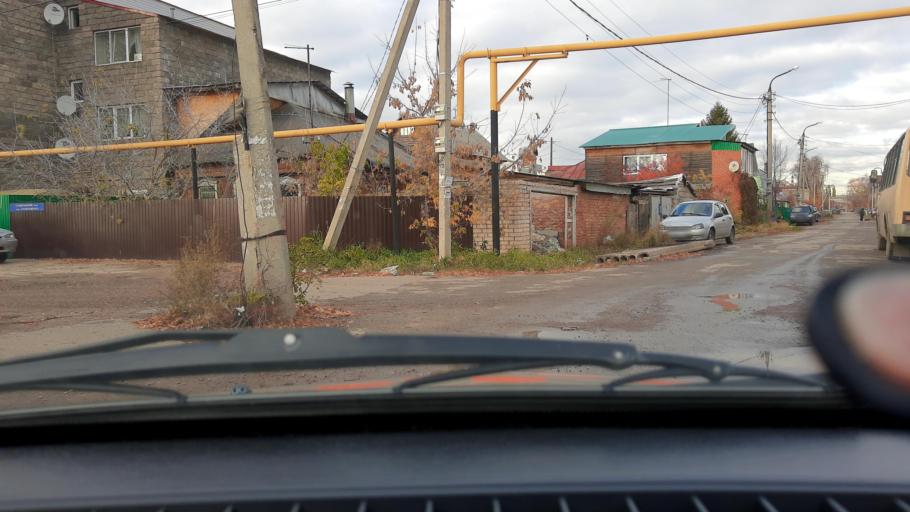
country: RU
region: Bashkortostan
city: Ufa
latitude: 54.7780
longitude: 56.0642
